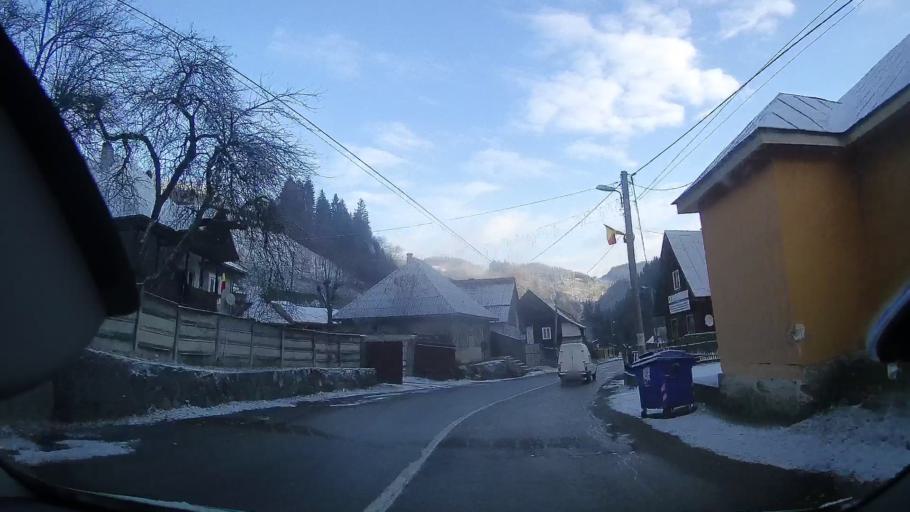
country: RO
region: Alba
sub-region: Comuna Scarisoara
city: Scarisoara
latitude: 46.4571
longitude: 22.8769
